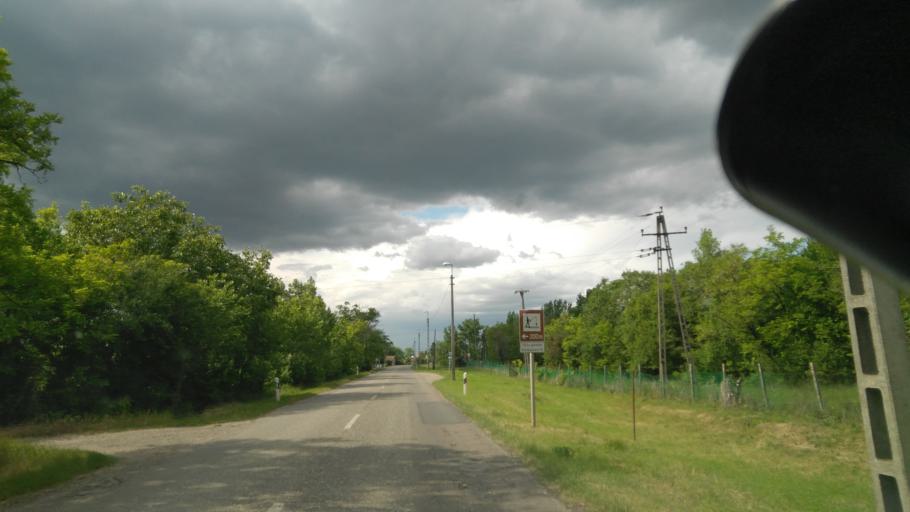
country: HU
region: Bekes
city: Oroshaza
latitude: 46.5837
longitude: 20.6461
